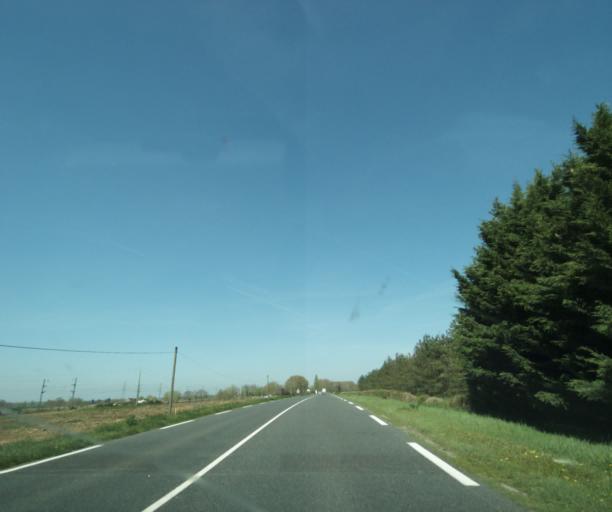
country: FR
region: Bourgogne
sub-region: Departement de la Nievre
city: Chantenay-Saint-Imbert
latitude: 46.6812
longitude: 3.2268
